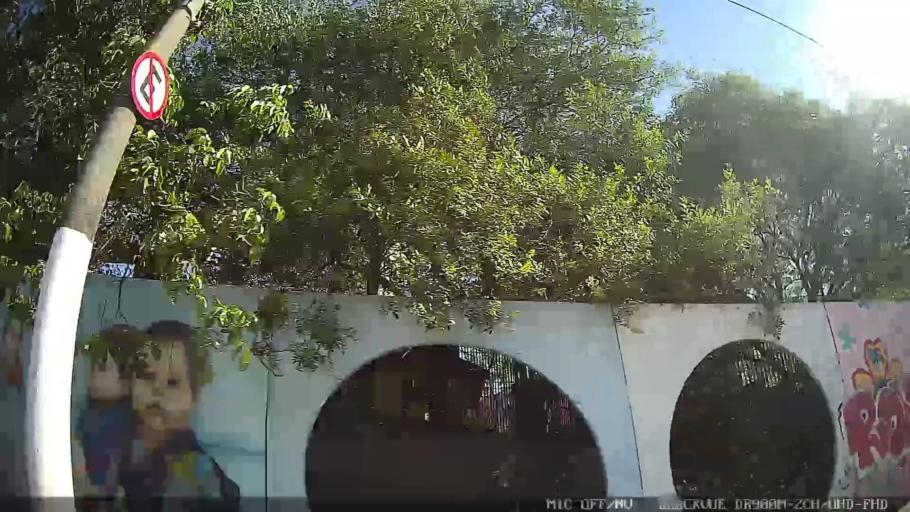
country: BR
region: Sao Paulo
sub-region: Guarulhos
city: Guarulhos
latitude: -23.5359
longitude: -46.4916
